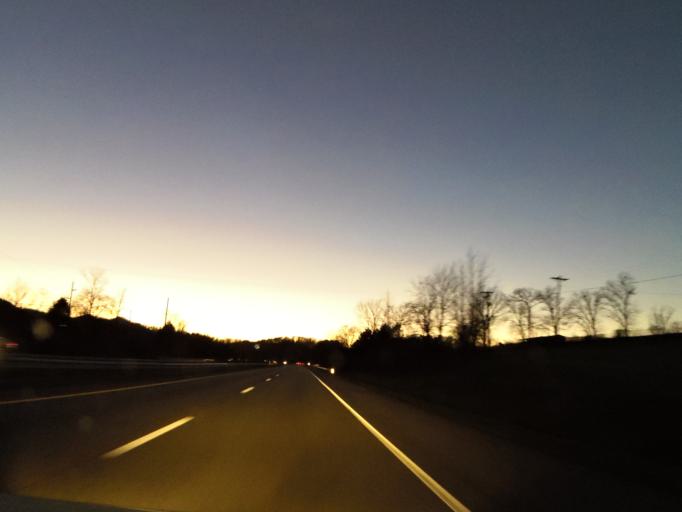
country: US
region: Tennessee
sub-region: Cocke County
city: Newport
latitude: 35.9683
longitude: -83.2339
